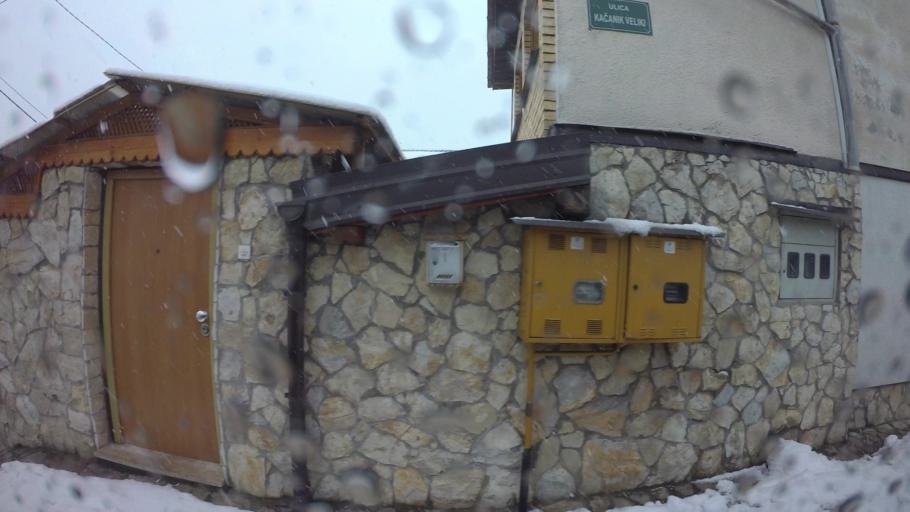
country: BA
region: Federation of Bosnia and Herzegovina
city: Kobilja Glava
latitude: 43.8549
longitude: 18.4401
